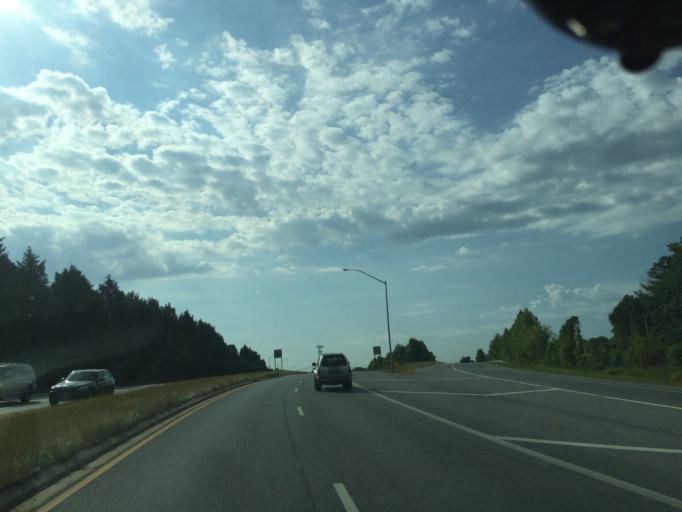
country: US
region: Maryland
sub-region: Baltimore County
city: Reisterstown
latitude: 39.4769
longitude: -76.8440
